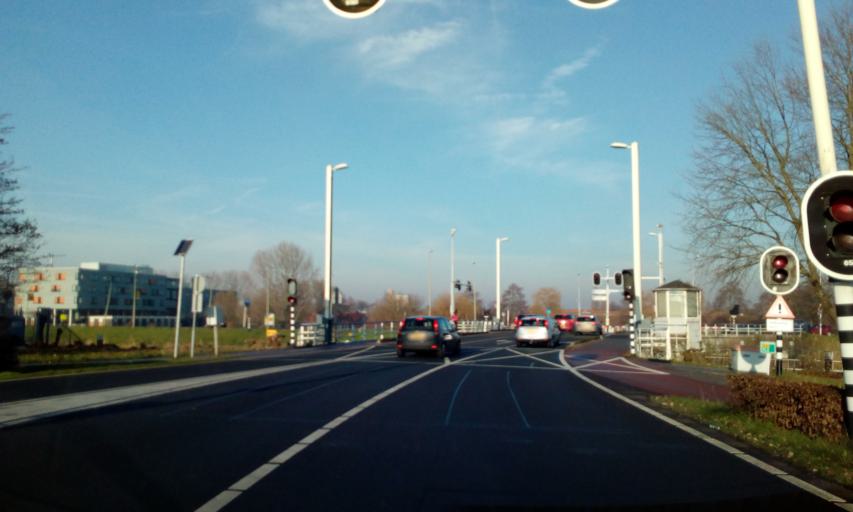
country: NL
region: South Holland
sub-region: Gemeente Gouda
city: Gouda
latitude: 52.0062
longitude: 4.7211
